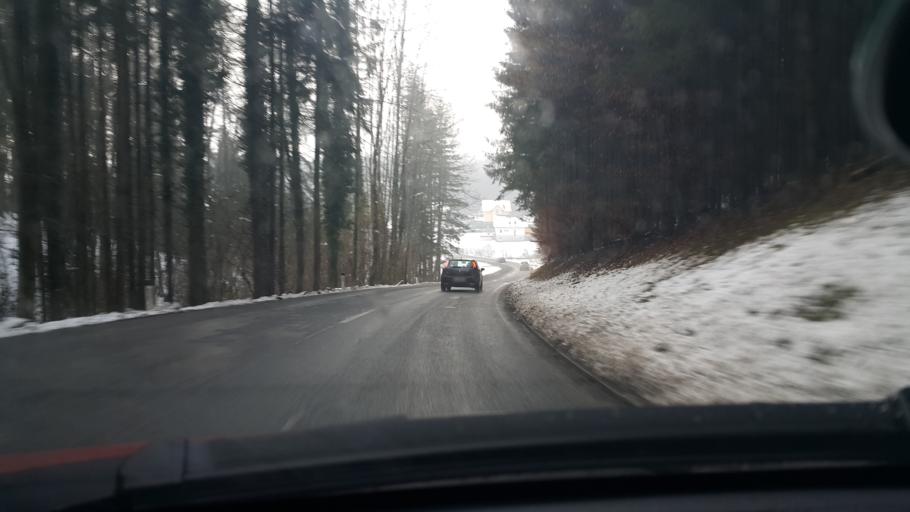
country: AT
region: Styria
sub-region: Politischer Bezirk Graz-Umgebung
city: Hitzendorf
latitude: 47.0636
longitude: 15.3046
